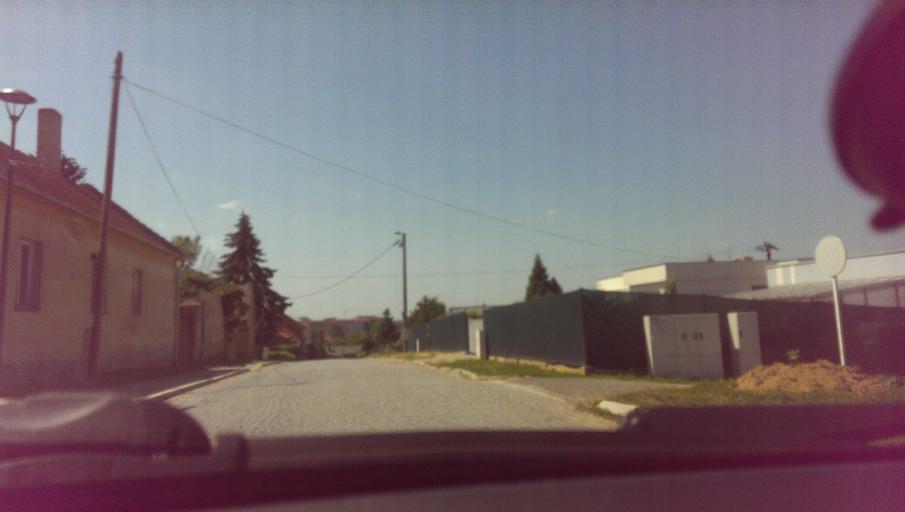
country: CZ
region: Zlin
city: Kunovice
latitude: 49.0638
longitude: 17.4867
